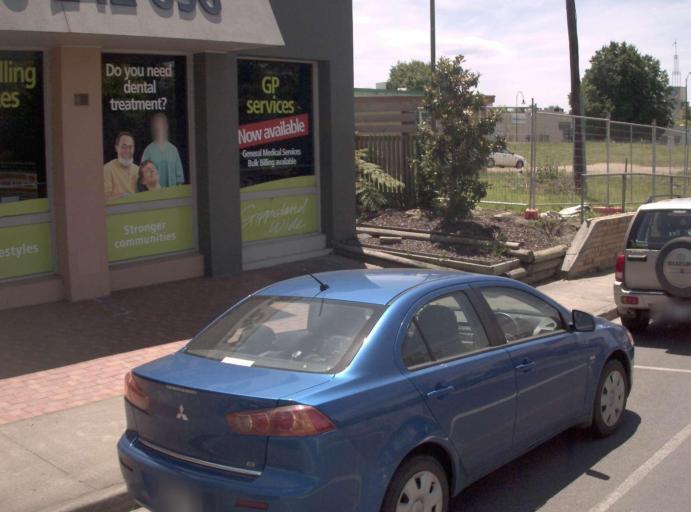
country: AU
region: Victoria
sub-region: Latrobe
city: Traralgon
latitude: -38.1962
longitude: 146.5411
